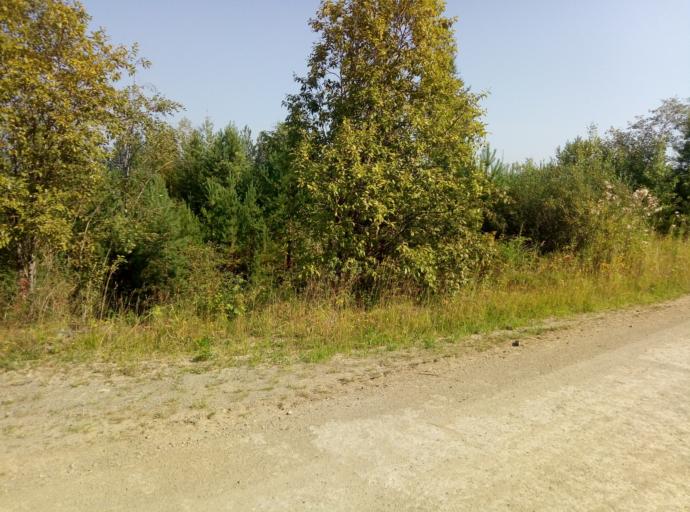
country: RU
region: Sverdlovsk
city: Rudnichnyy
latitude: 59.7289
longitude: 60.3352
